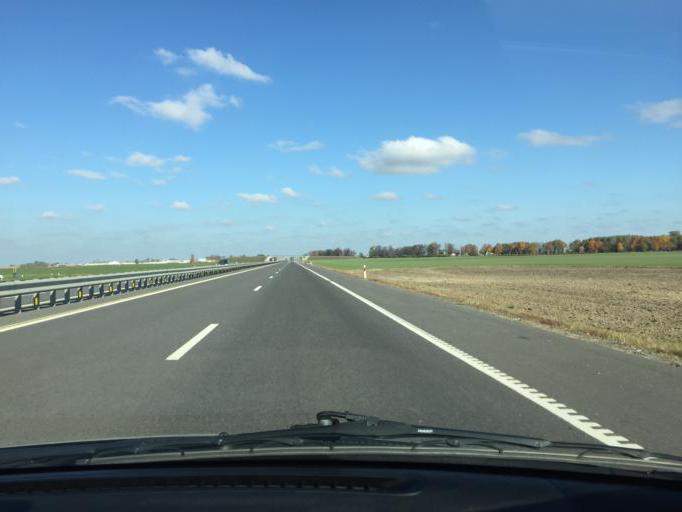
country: BY
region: Minsk
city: Slutsk
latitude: 53.0592
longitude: 27.5444
